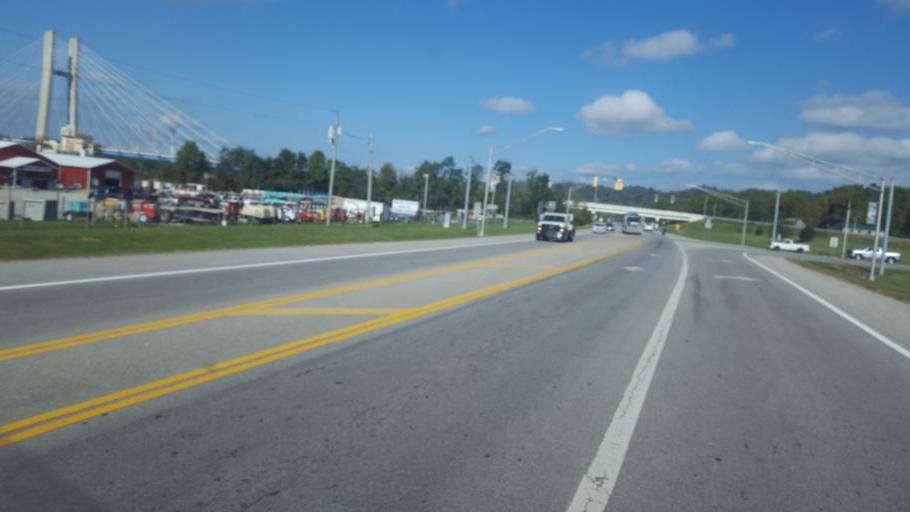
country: US
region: Ohio
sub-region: Brown County
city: Aberdeen
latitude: 38.6834
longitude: -83.7751
